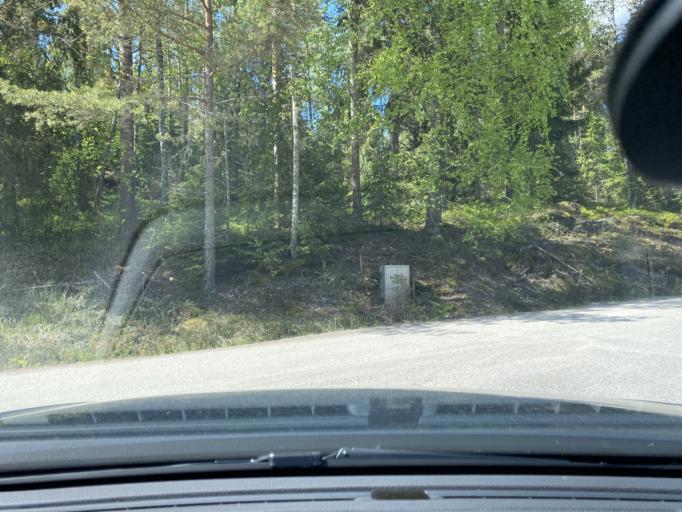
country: FI
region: Varsinais-Suomi
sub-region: Salo
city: Halikko
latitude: 60.3319
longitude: 22.9415
